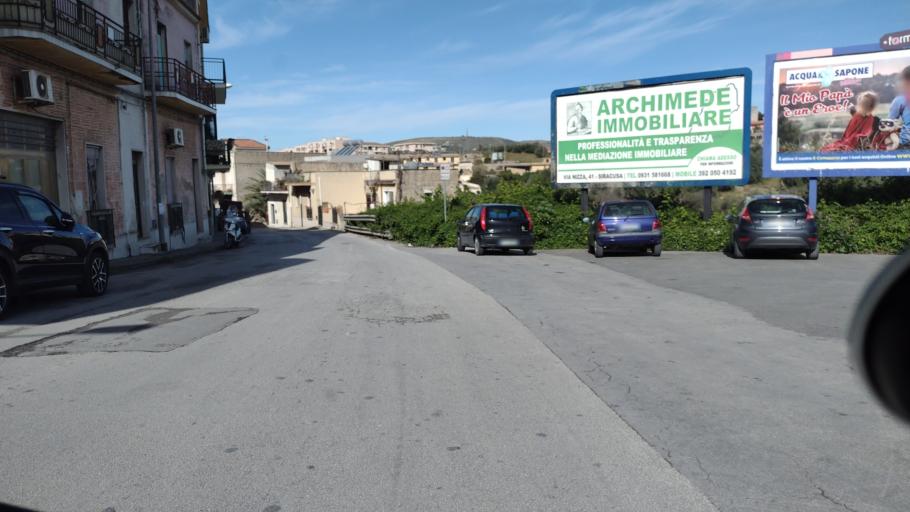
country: IT
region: Sicily
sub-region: Provincia di Siracusa
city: Noto
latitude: 36.8949
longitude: 15.0677
